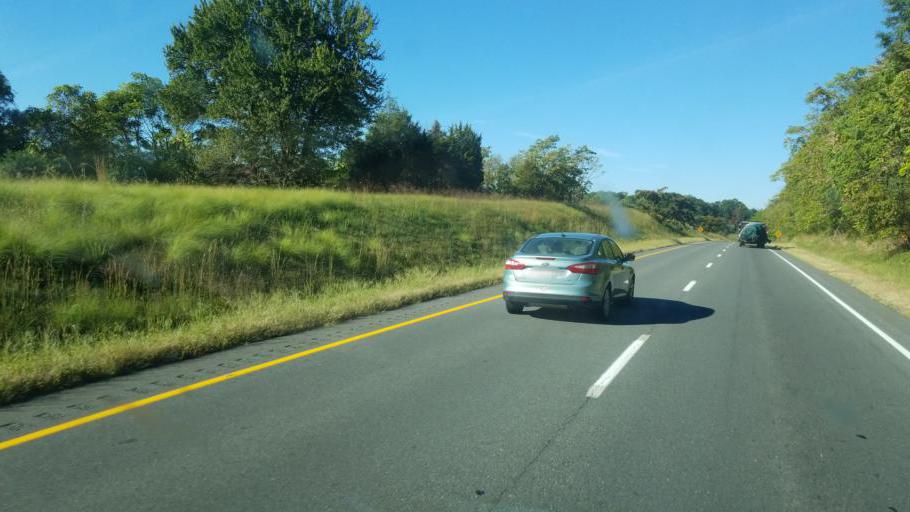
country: US
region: Virginia
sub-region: Culpeper County
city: Merrimac
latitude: 38.4509
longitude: -78.0849
